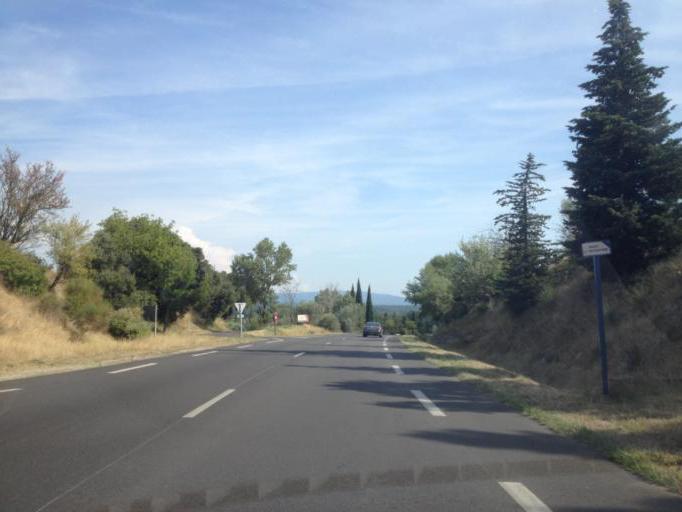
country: FR
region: Provence-Alpes-Cote d'Azur
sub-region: Departement du Vaucluse
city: Vacqueyras
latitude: 44.1280
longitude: 4.9973
